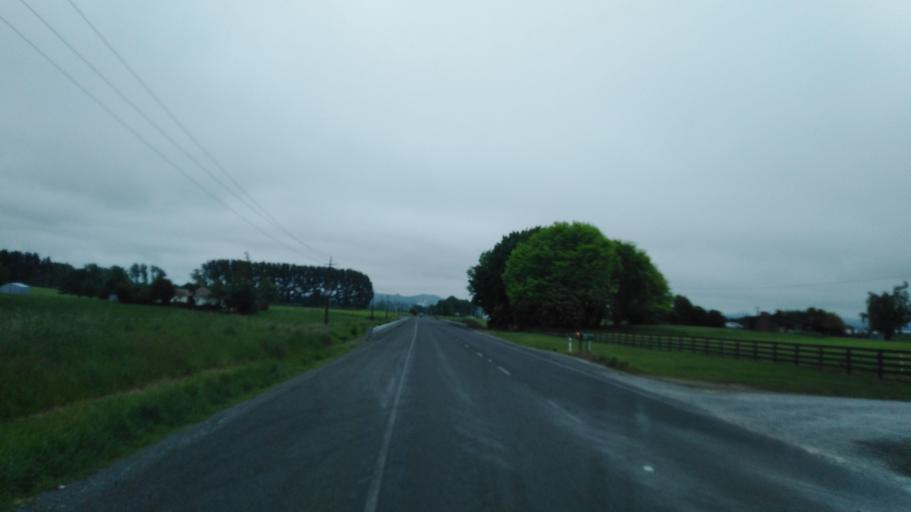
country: NZ
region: Bay of Plenty
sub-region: Rotorua District
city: Rotorua
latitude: -38.3892
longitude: 176.3404
